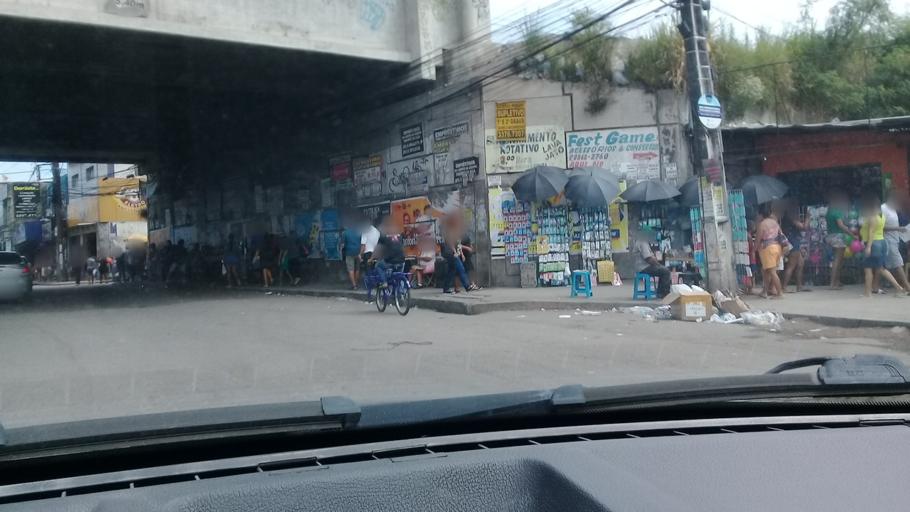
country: BR
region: Pernambuco
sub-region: Jaboatao Dos Guararapes
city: Jaboatao
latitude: -8.1612
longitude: -34.9272
